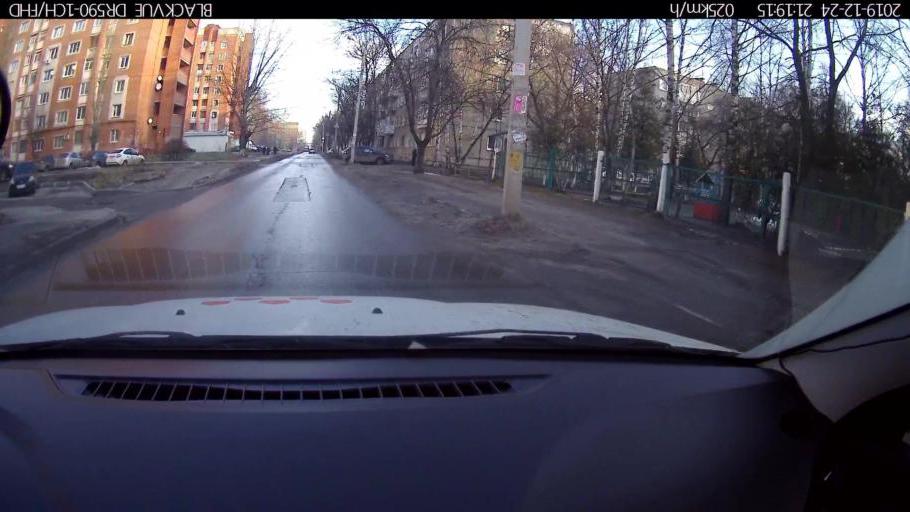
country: RU
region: Nizjnij Novgorod
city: Gorbatovka
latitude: 56.2665
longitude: 43.8810
